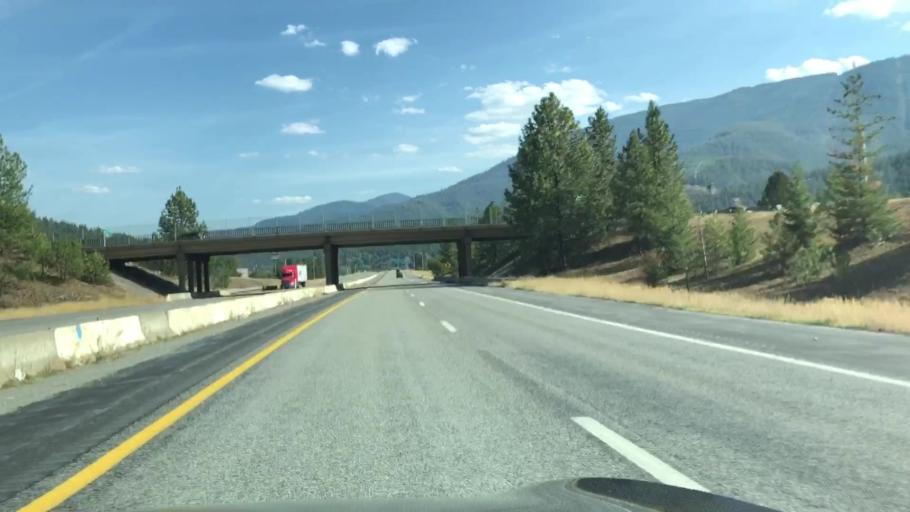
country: US
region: Idaho
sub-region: Shoshone County
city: Kellogg
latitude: 47.5464
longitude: -116.1340
